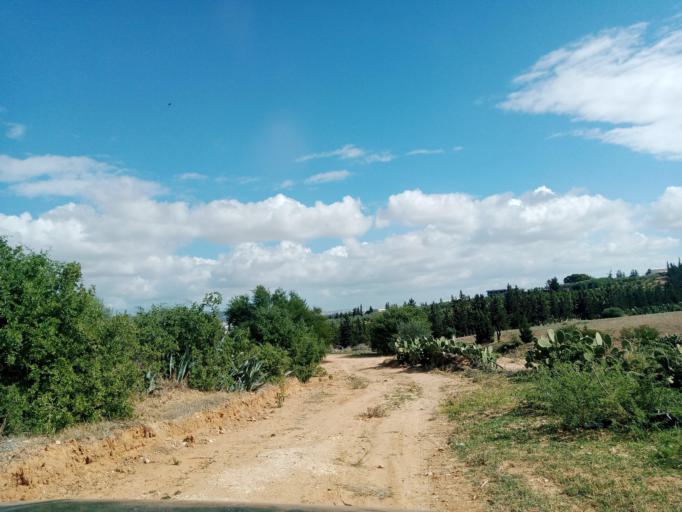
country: TN
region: Tunis
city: Oued Lill
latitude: 36.8177
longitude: 10.0050
